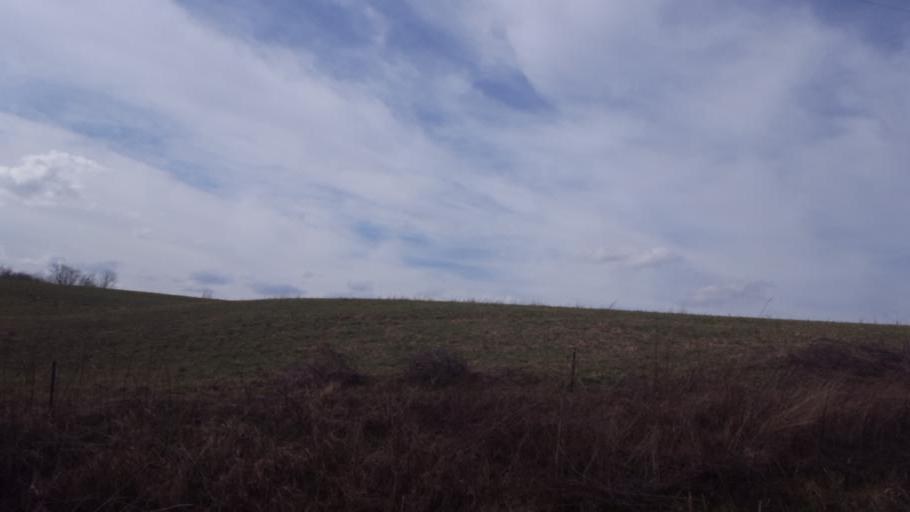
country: US
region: Ohio
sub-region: Knox County
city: Fredericktown
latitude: 40.5041
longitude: -82.4245
